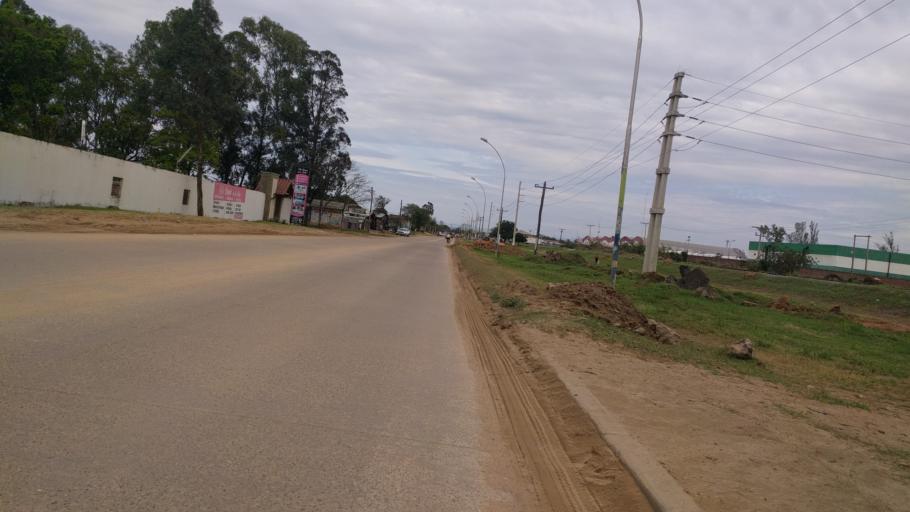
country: BO
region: Santa Cruz
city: Santa Cruz de la Sierra
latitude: -17.8487
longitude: -63.1780
